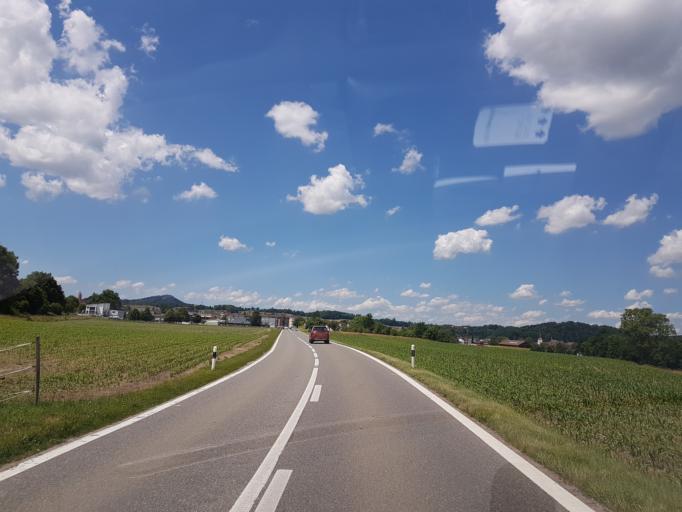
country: CH
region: Aargau
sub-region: Bezirk Baden
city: Mellingen
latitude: 47.4106
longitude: 8.2816
